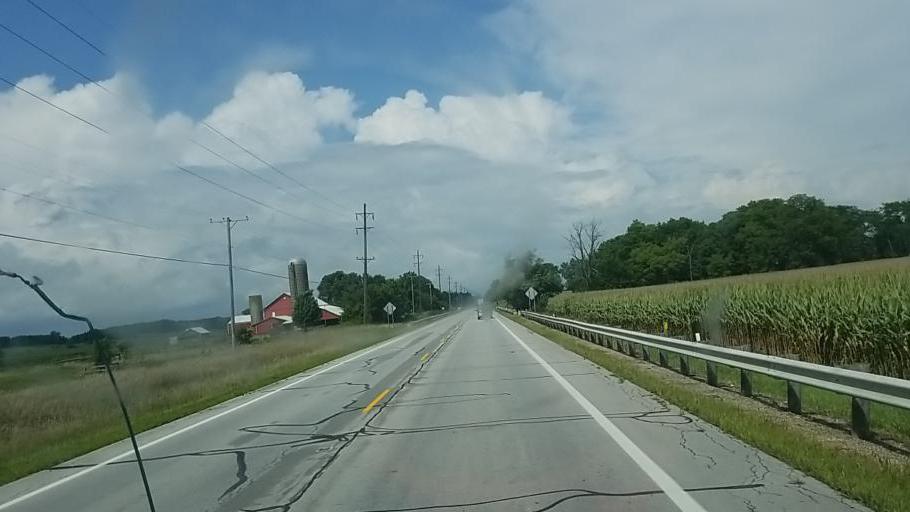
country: US
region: Ohio
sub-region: Champaign County
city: Urbana
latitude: 40.1575
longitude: -83.7456
